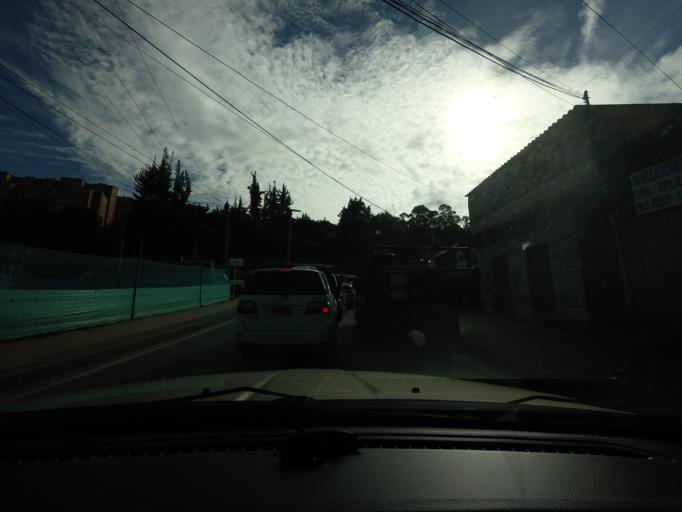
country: CO
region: Cundinamarca
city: La Calera
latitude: 4.7603
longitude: -74.0269
